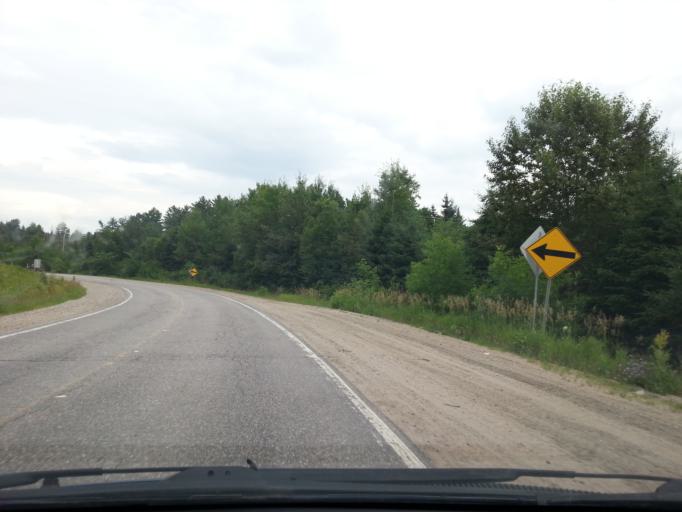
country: CA
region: Quebec
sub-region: Outaouais
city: Maniwaki
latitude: 46.0763
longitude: -76.0759
